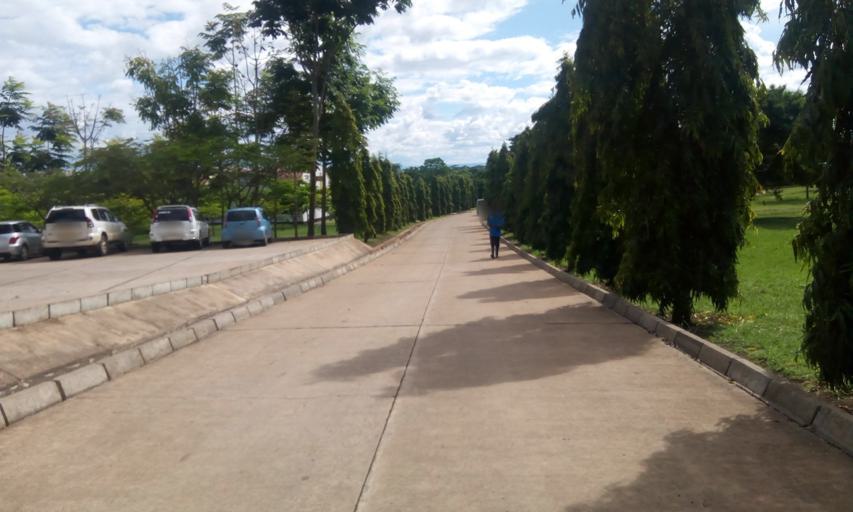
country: TZ
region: Arusha
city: Usa River
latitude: -3.4002
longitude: 36.7970
